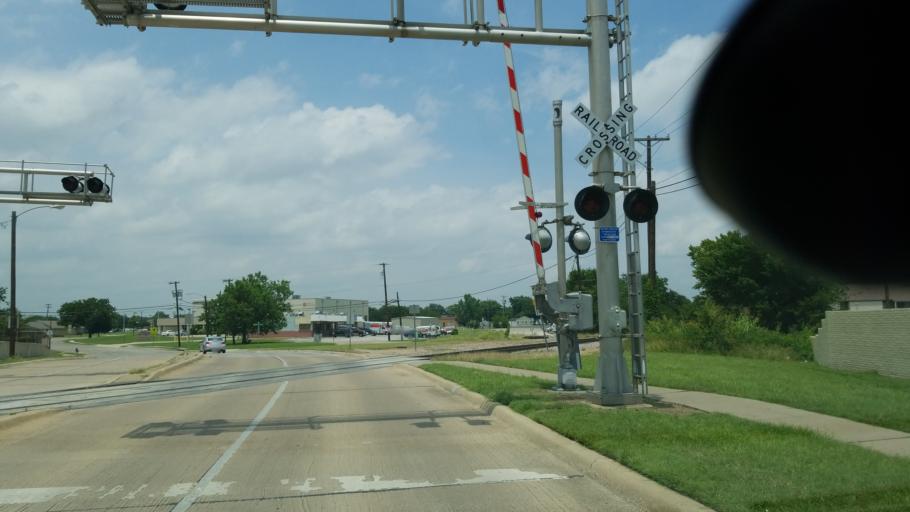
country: US
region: Texas
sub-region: Dallas County
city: Irving
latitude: 32.8268
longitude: -96.9424
